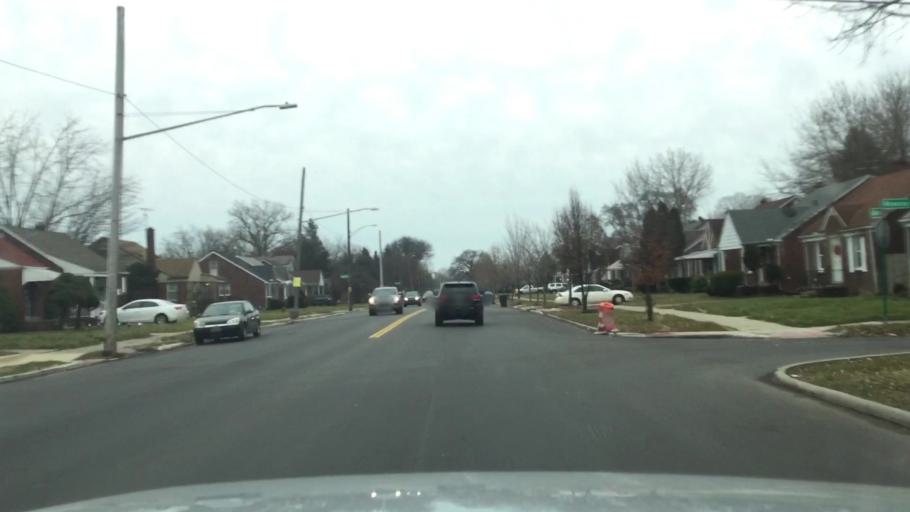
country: US
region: Michigan
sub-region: Wayne County
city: Grosse Pointe
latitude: 42.4014
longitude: -82.9267
